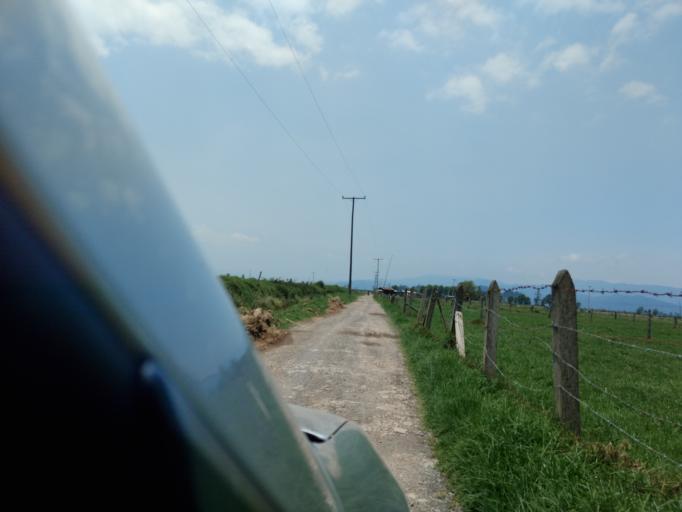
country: CO
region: Boyaca
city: Raquira
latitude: 5.4988
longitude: -73.7093
